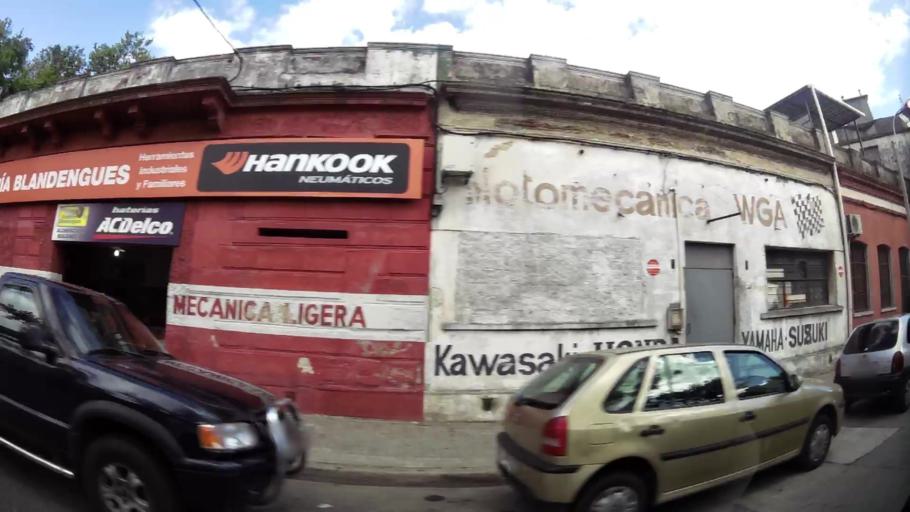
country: UY
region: Montevideo
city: Montevideo
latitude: -34.8835
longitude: -56.1822
